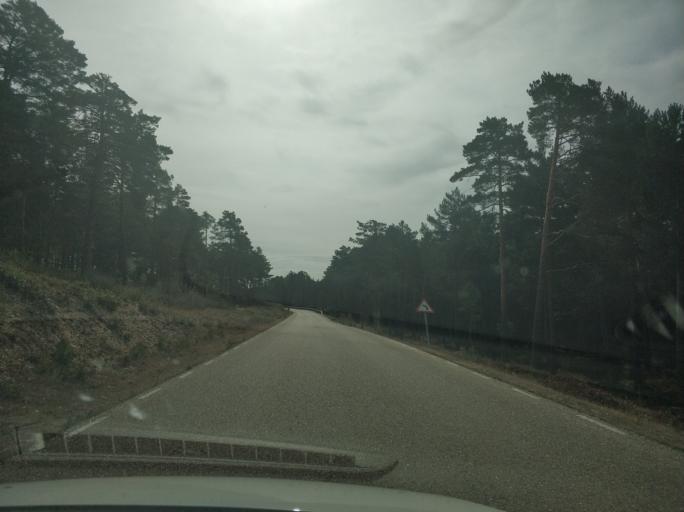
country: ES
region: Castille and Leon
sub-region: Provincia de Soria
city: Navaleno
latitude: 41.8553
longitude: -2.9665
